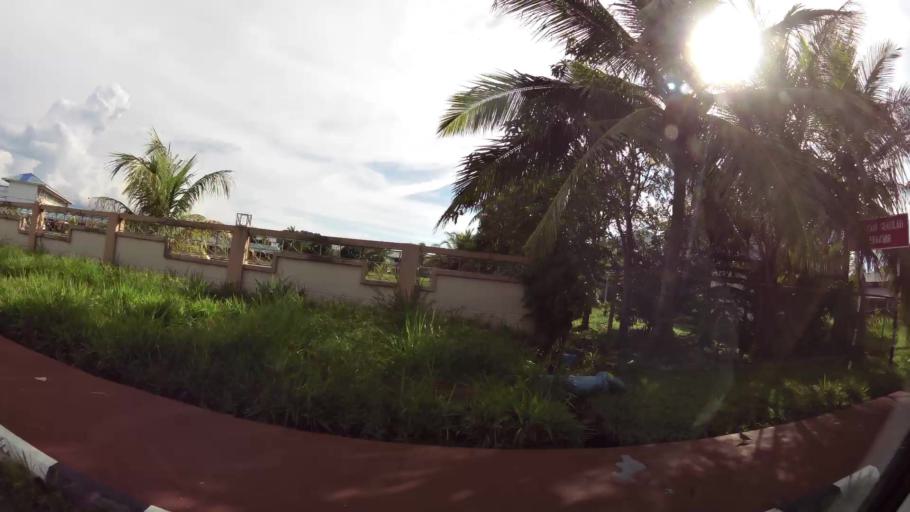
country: BN
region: Brunei and Muara
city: Bandar Seri Begawan
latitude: 4.9701
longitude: 115.0289
